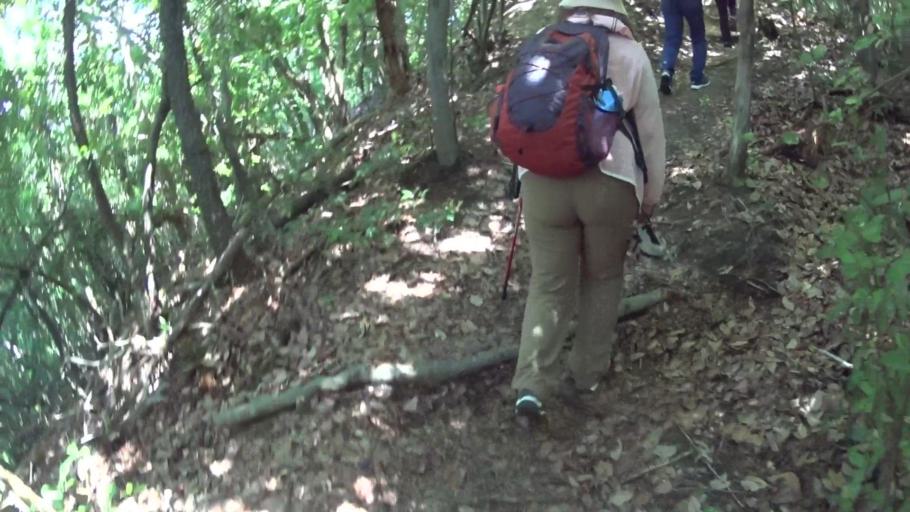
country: JP
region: Kyoto
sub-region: Kyoto-shi
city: Kamigyo-ku
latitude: 35.0391
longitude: 135.7983
